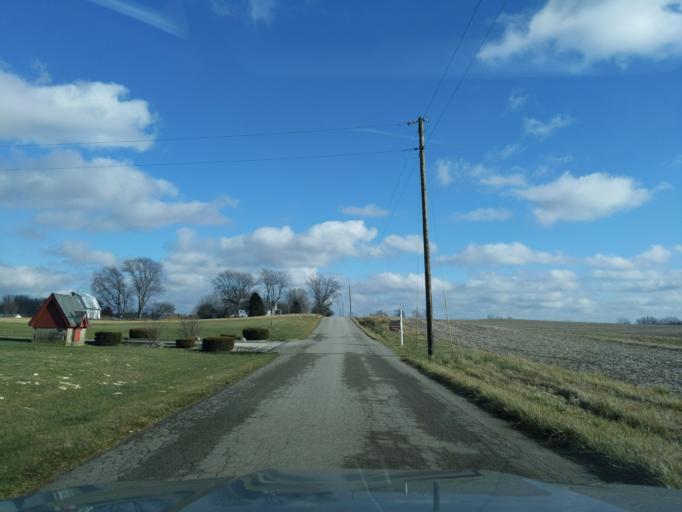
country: US
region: Indiana
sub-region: Decatur County
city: Greensburg
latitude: 39.2781
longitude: -85.4756
